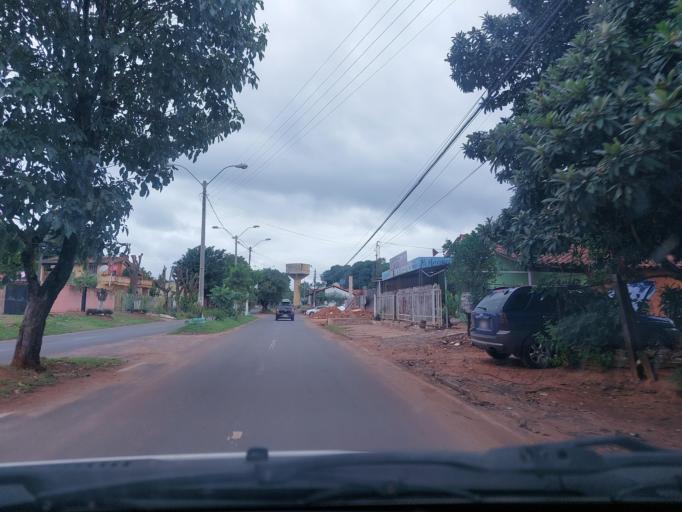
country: PY
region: San Pedro
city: Guayaybi
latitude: -24.6707
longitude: -56.4424
